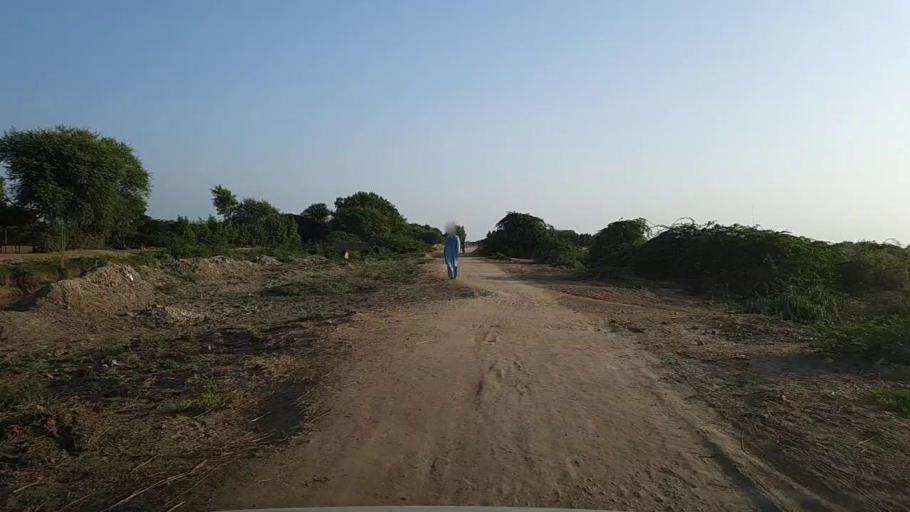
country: PK
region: Sindh
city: Kario
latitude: 24.7152
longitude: 68.6672
